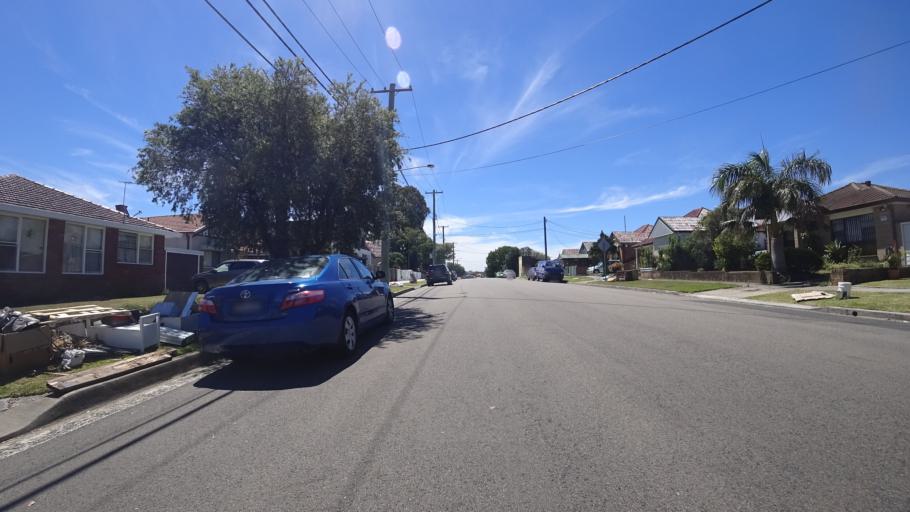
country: AU
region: New South Wales
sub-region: Rockdale
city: Bexley
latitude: -33.9604
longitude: 151.1252
